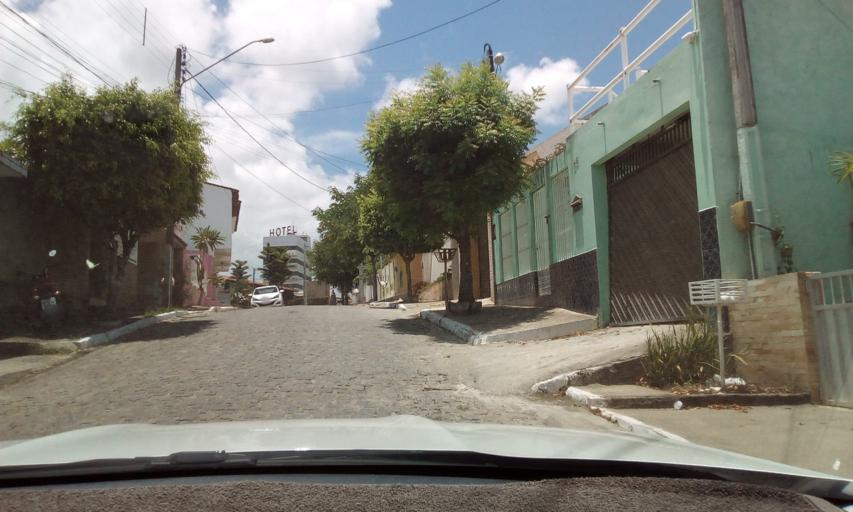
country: BR
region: Pernambuco
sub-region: Bonito
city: Bonito
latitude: -8.4734
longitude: -35.7279
